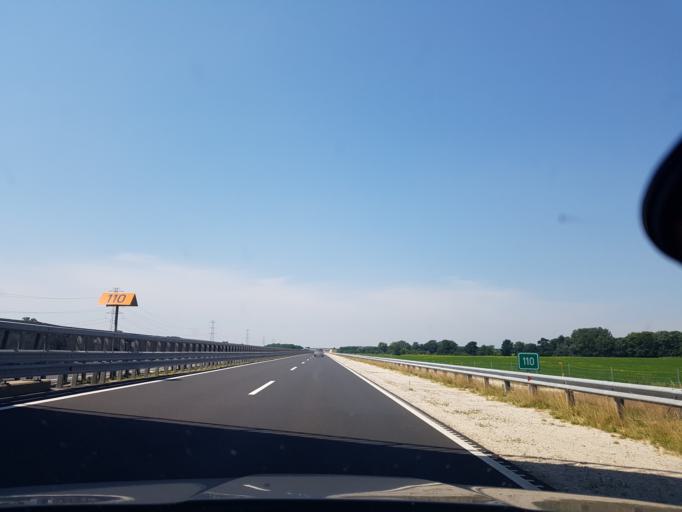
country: HU
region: Vas
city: Repcelak
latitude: 47.3798
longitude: 16.9608
